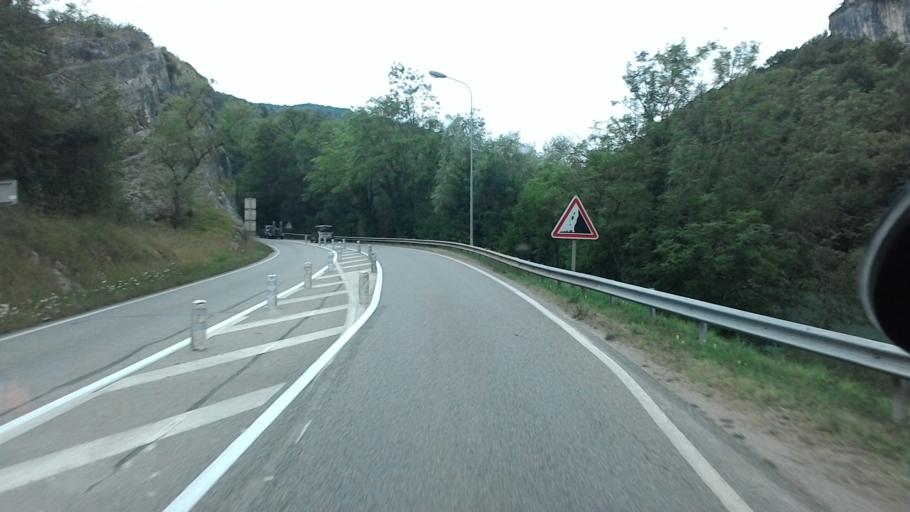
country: FR
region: Rhone-Alpes
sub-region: Departement de la Savoie
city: Yenne
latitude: 45.7054
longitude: 5.7509
